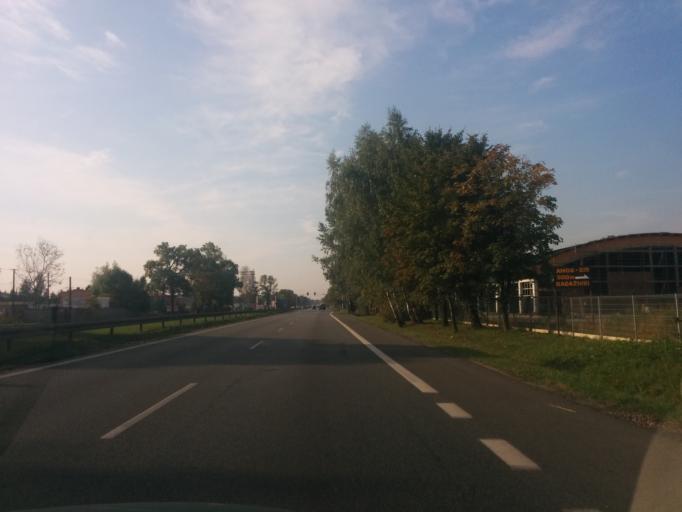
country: PL
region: Masovian Voivodeship
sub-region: Powiat piaseczynski
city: Tarczyn
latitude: 52.0412
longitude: 20.8620
